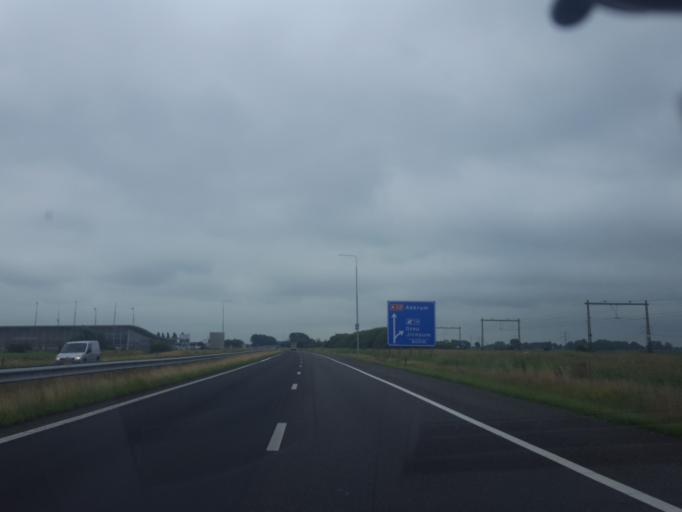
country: NL
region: Friesland
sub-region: Gemeente Boarnsterhim
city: Grou
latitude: 53.1028
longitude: 5.8168
